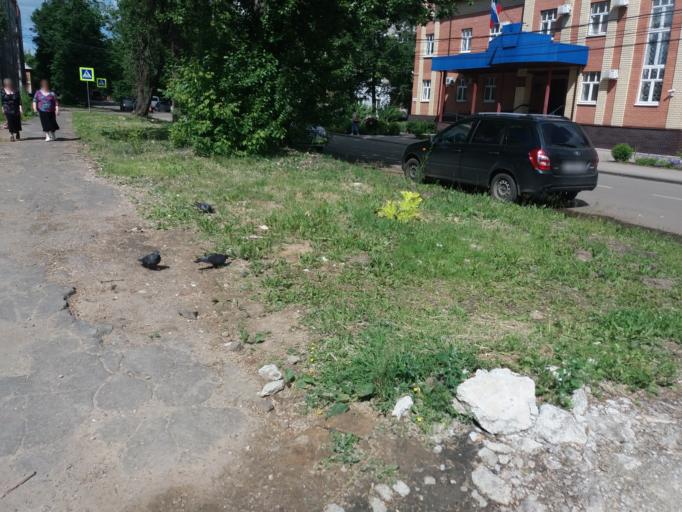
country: RU
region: Jaroslavl
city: Yaroslavl
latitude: 57.6405
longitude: 39.8407
